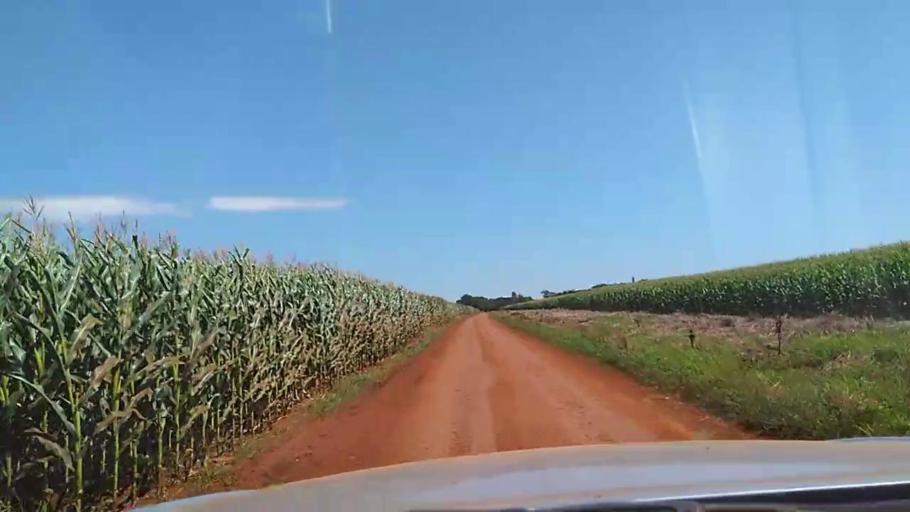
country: PY
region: Alto Parana
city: Naranjal
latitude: -25.9492
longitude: -55.1173
